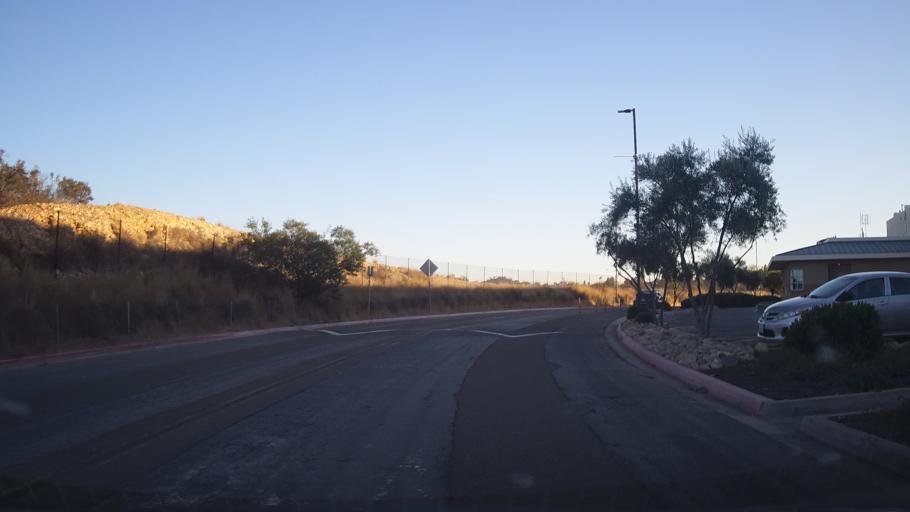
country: US
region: California
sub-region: San Diego County
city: Santee
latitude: 32.8167
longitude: -117.0027
